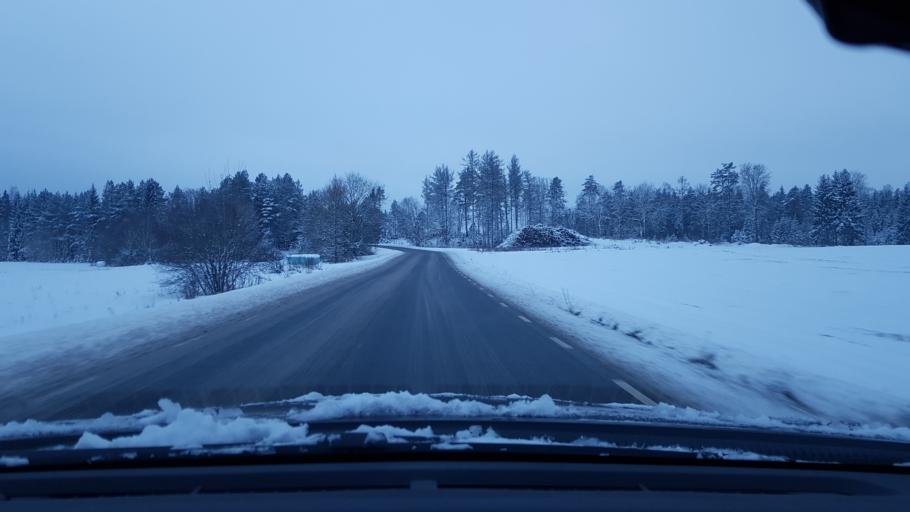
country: EE
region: Raplamaa
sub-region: Rapla vald
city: Rapla
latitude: 58.9464
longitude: 24.6624
